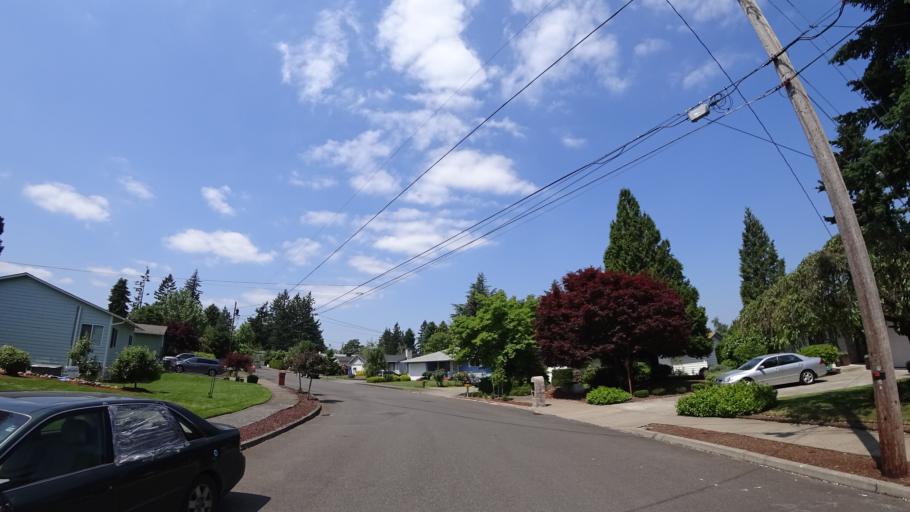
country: US
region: Oregon
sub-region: Multnomah County
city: Fairview
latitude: 45.5350
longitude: -122.4996
